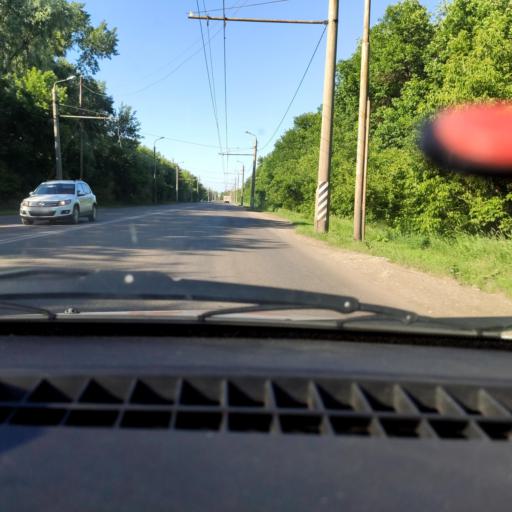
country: RU
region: Bashkortostan
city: Sterlitamak
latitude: 53.6573
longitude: 55.9219
